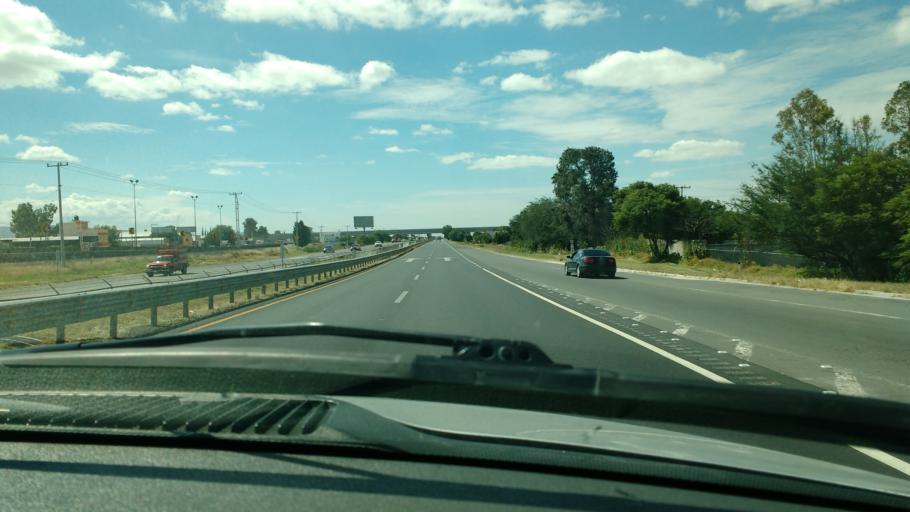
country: MX
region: Guanajuato
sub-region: Apaseo el Grande
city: La Labor
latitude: 20.5371
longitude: -100.7009
